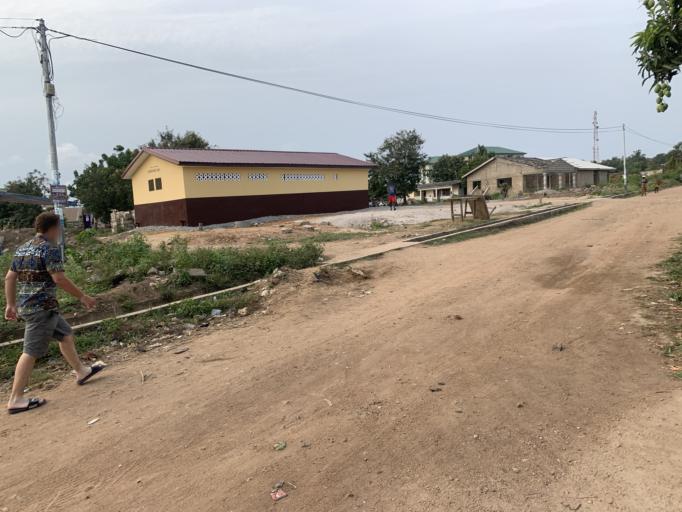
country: GH
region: Central
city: Winneba
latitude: 5.3544
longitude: -0.6291
